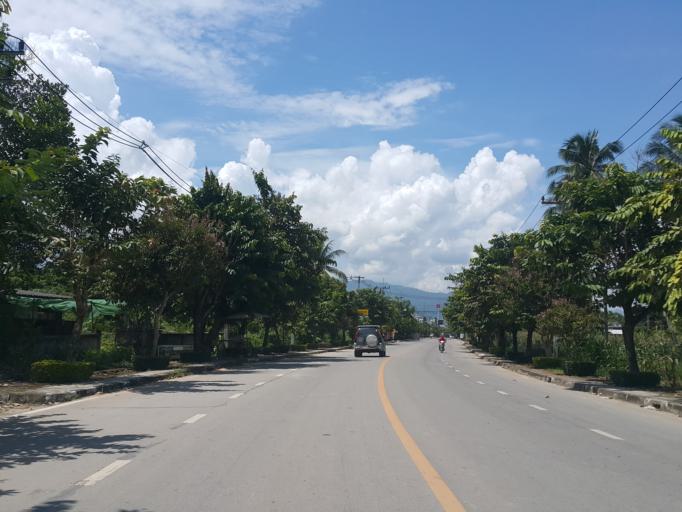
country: TH
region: Chiang Mai
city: Phrao
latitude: 19.3680
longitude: 99.2090
